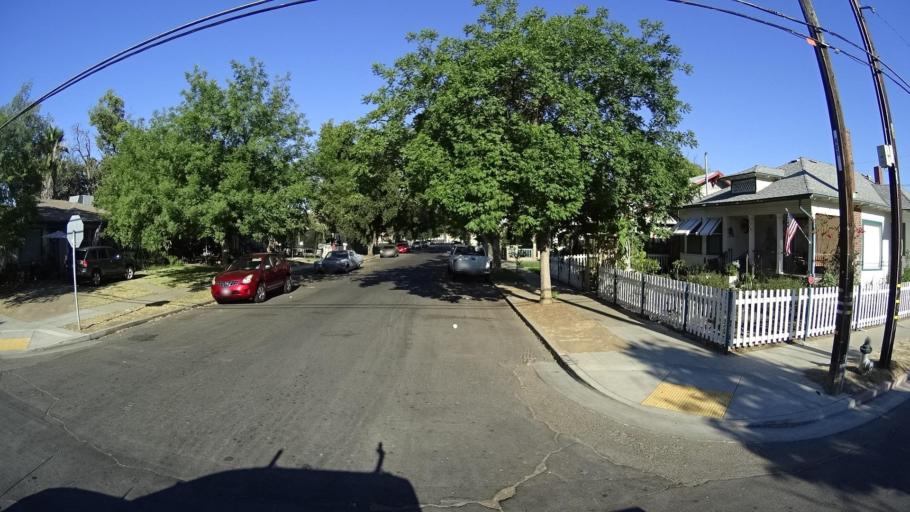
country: US
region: California
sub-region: Fresno County
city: Fresno
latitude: 36.7496
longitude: -119.7793
